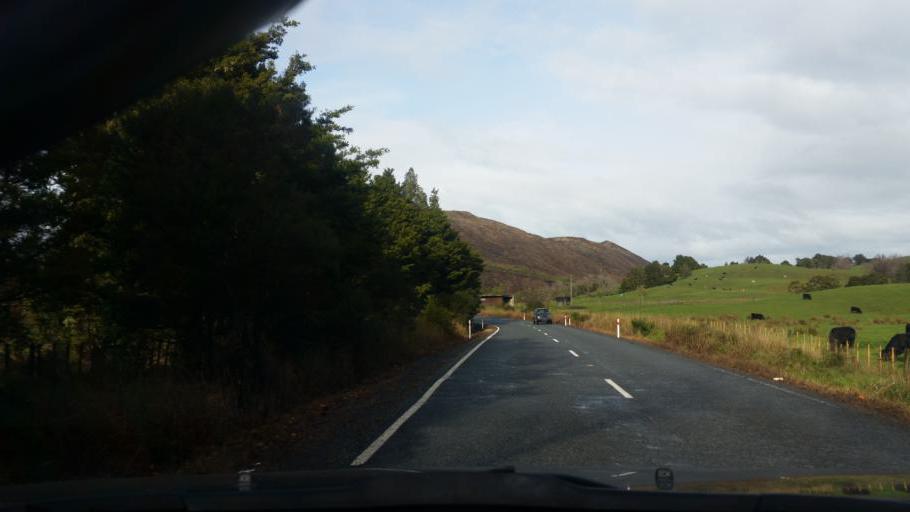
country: NZ
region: Northland
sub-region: Kaipara District
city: Dargaville
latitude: -35.7562
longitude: 173.9012
